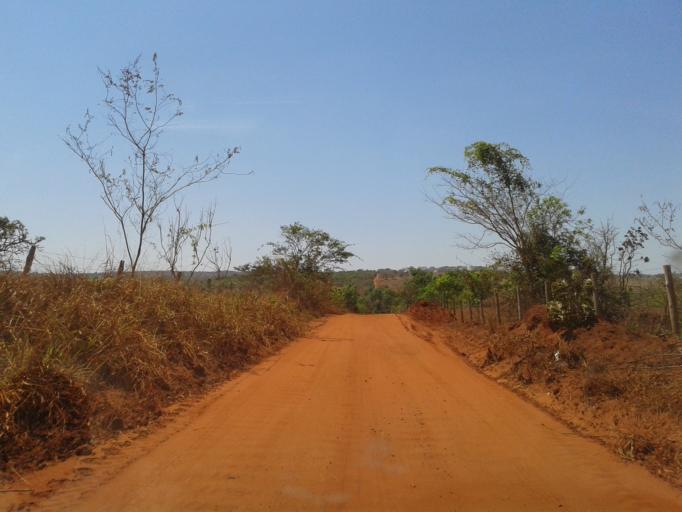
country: BR
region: Minas Gerais
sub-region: Ituiutaba
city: Ituiutaba
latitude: -19.0650
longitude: -49.3255
